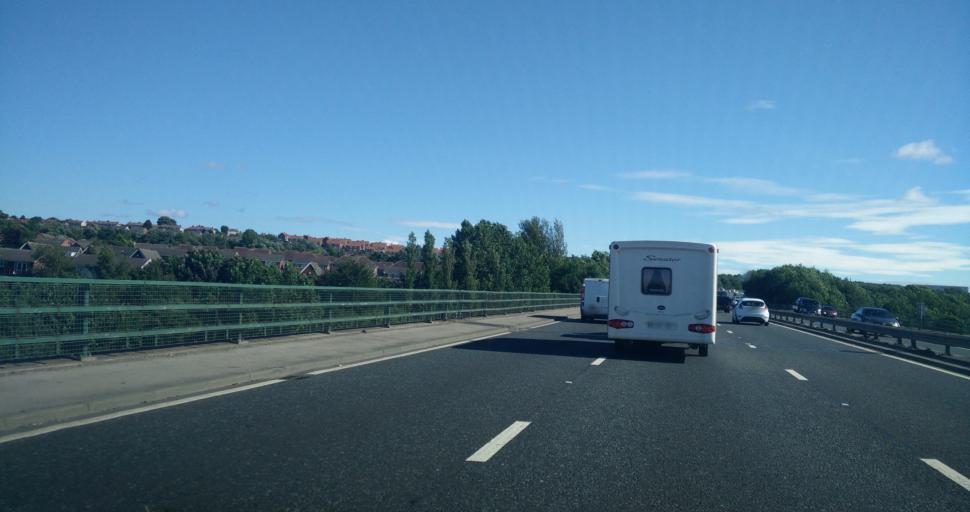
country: GB
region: England
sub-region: South Tyneside
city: The Boldons
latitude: 54.9044
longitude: -1.4582
